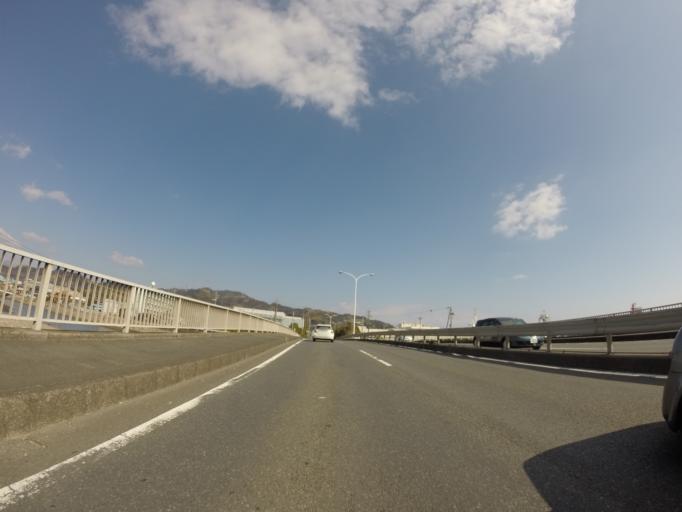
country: JP
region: Shizuoka
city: Shizuoka-shi
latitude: 35.0361
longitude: 138.4998
